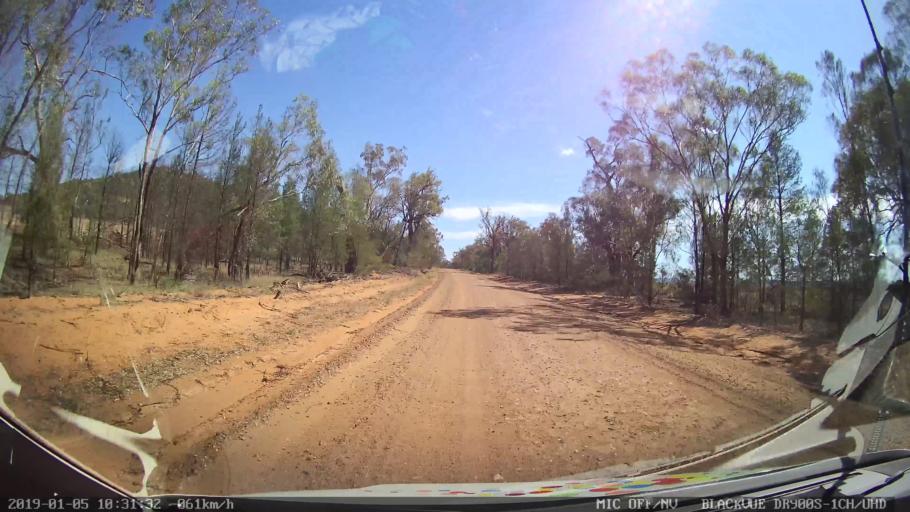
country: AU
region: New South Wales
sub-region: Gilgandra
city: Gilgandra
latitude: -31.5235
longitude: 148.9280
